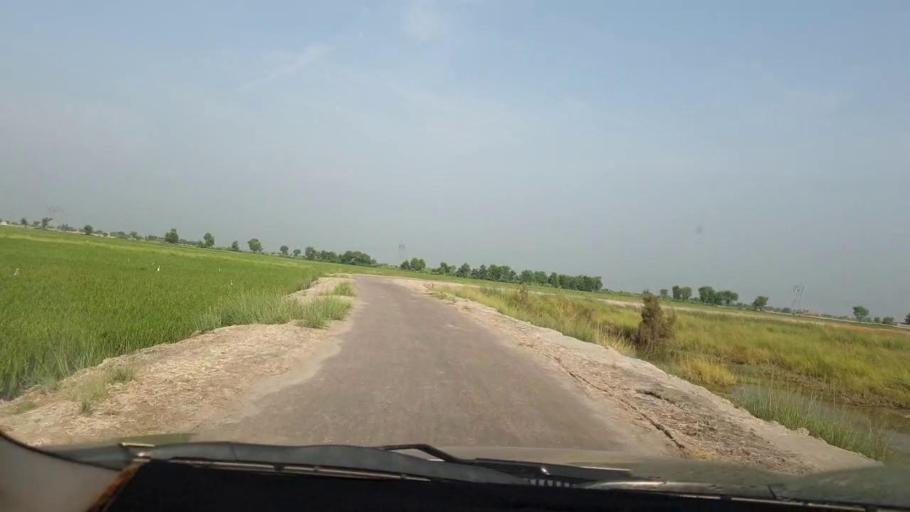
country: PK
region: Sindh
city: Goth Garelo
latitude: 27.4685
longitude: 68.0791
